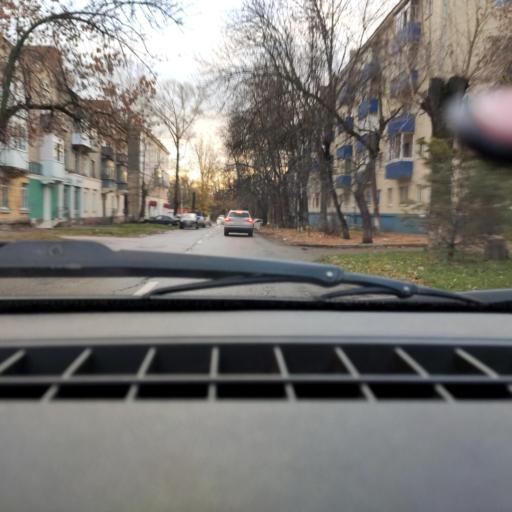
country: RU
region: Bashkortostan
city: Ufa
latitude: 54.8207
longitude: 56.0931
